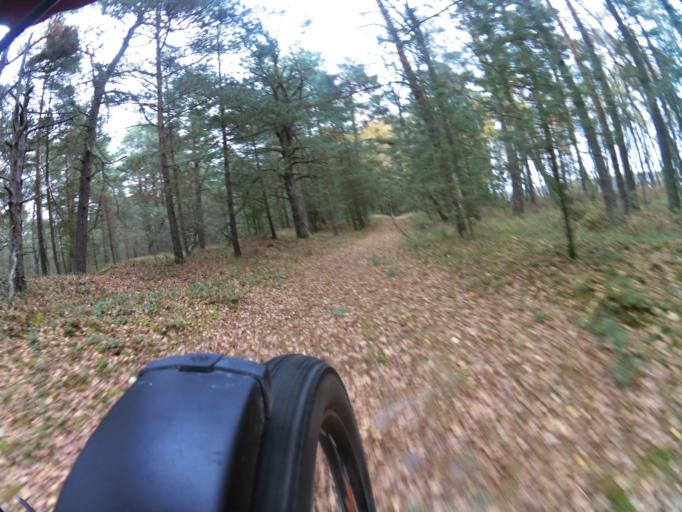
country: PL
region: Pomeranian Voivodeship
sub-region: Powiat leborski
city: Leba
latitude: 54.7675
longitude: 17.6140
